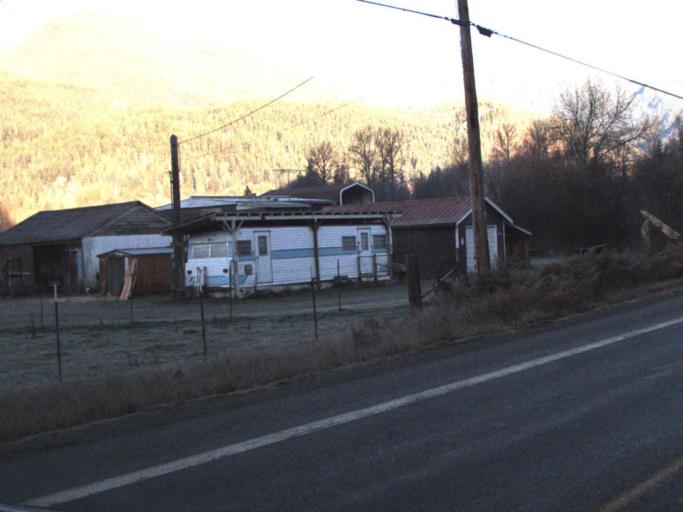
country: US
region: Washington
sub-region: Snohomish County
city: Darrington
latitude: 48.5339
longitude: -121.4301
